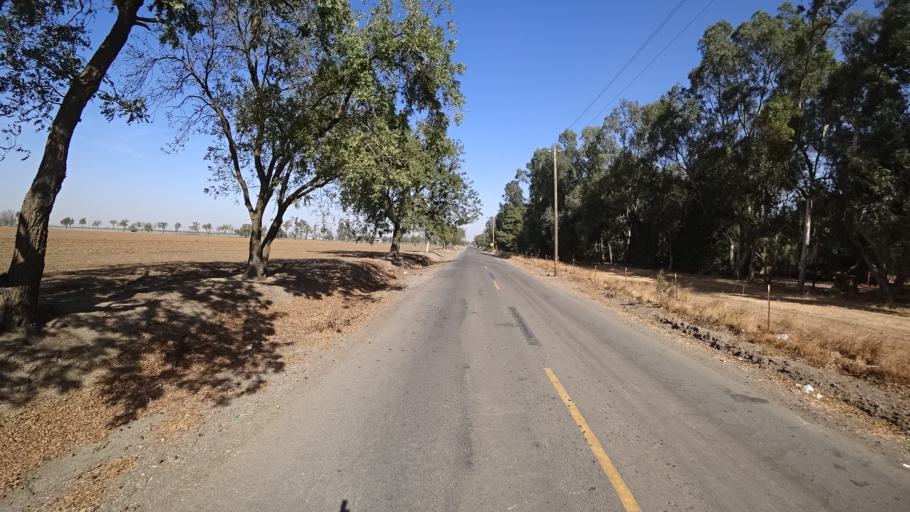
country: US
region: California
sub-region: Yolo County
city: Davis
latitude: 38.4925
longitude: -121.6956
